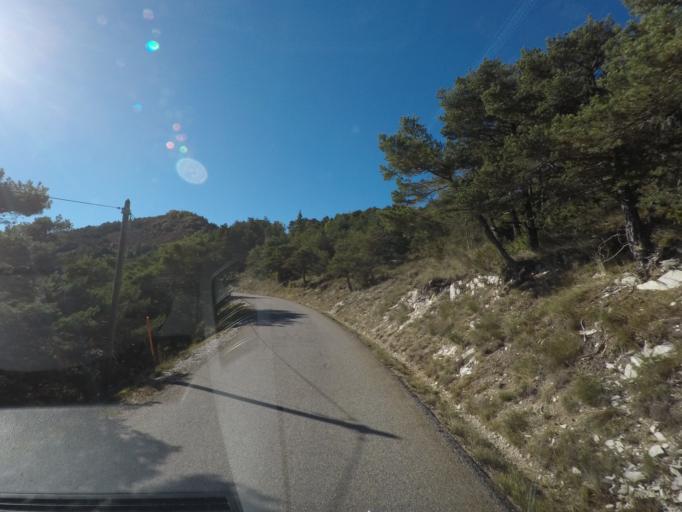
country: FR
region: Provence-Alpes-Cote d'Azur
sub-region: Departement des Hautes-Alpes
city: Serres
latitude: 44.4323
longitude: 5.5732
